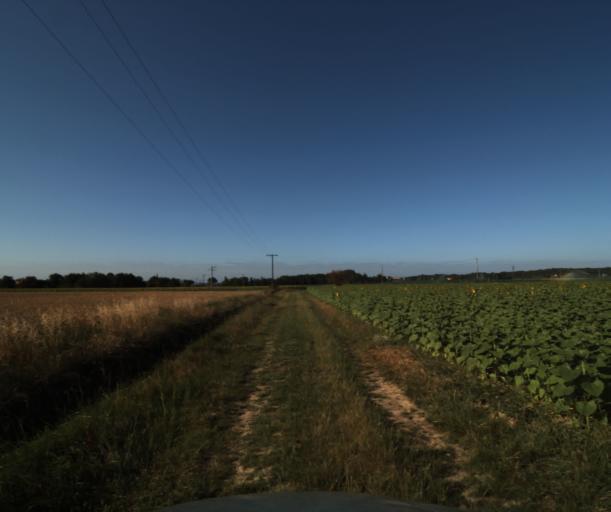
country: FR
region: Midi-Pyrenees
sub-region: Departement de la Haute-Garonne
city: Labarthe-sur-Leze
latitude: 43.4465
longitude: 1.3816
